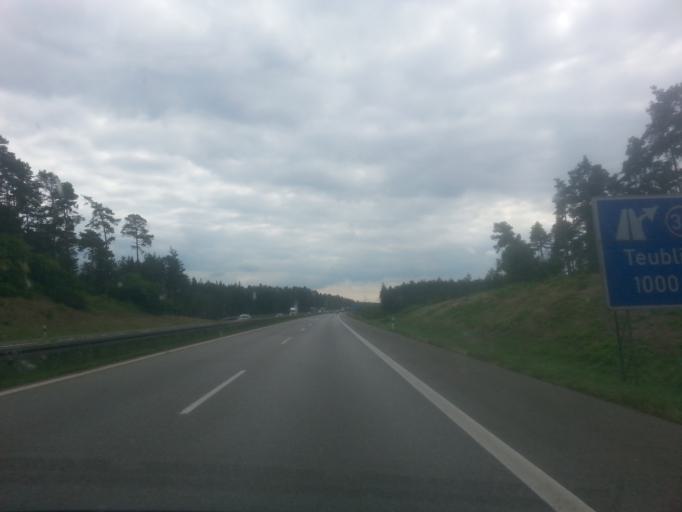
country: DE
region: Bavaria
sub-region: Upper Palatinate
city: Teublitz
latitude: 49.2316
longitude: 12.1318
